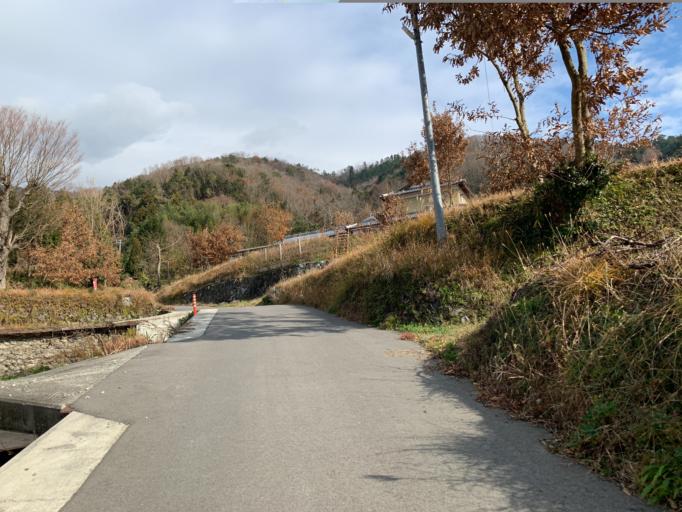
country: JP
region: Kyoto
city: Kameoka
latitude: 35.0532
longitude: 135.5806
